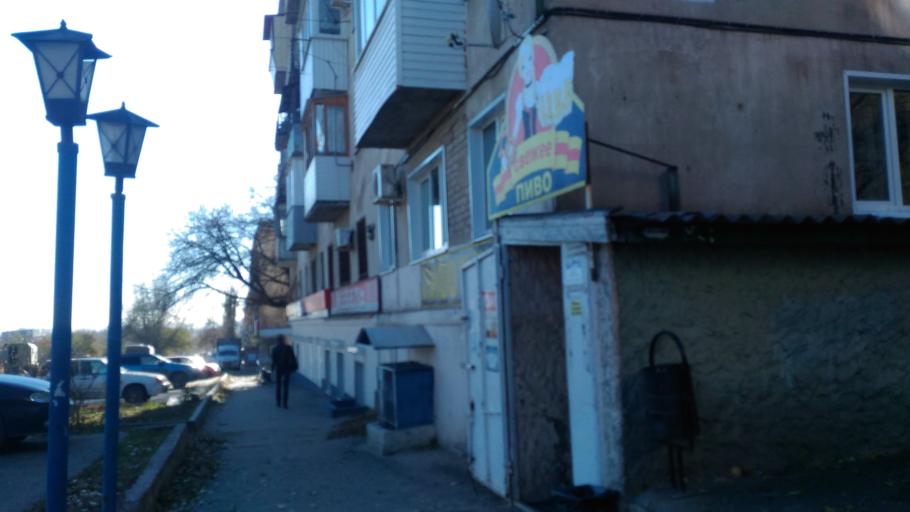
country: RU
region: Volgograd
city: Volgograd
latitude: 48.6630
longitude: 44.4389
